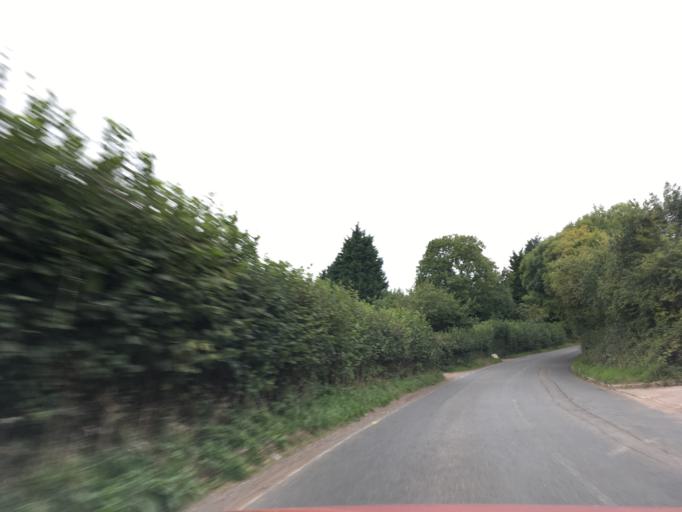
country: GB
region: Wales
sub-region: Newport
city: Marshfield
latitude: 51.5444
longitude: -3.0833
